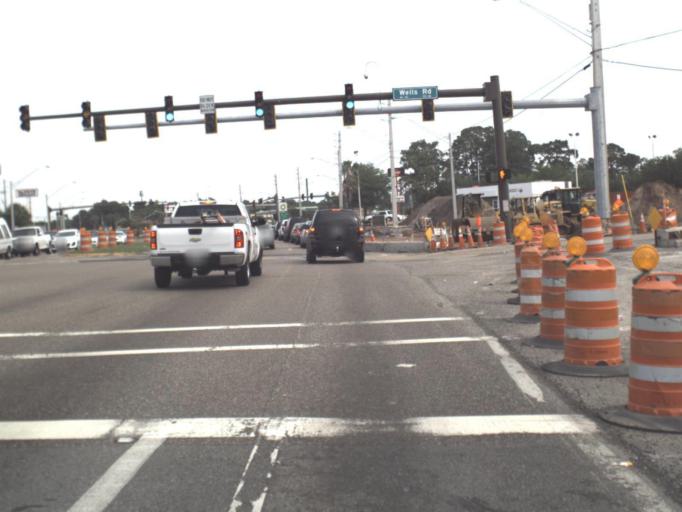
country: US
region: Florida
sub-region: Clay County
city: Orange Park
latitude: 30.1851
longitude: -81.7017
